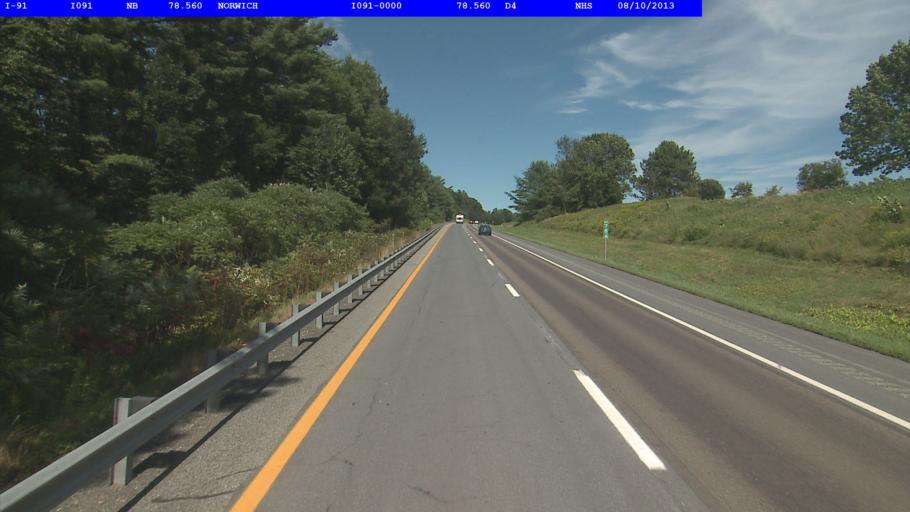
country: US
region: New Hampshire
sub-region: Grafton County
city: Hanover
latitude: 43.7457
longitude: -72.2578
